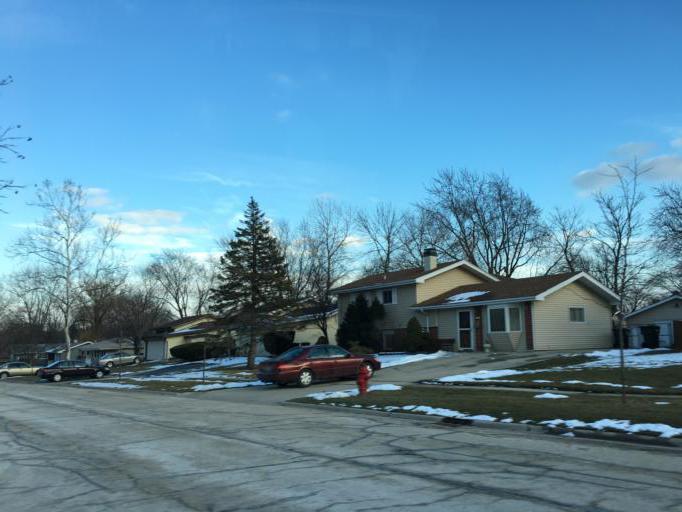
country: US
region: Illinois
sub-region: Cook County
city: Schaumburg
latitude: 42.0423
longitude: -88.0964
